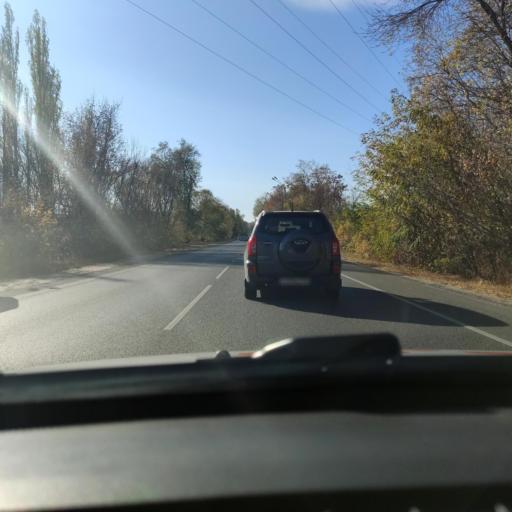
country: RU
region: Voronezj
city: Maslovka
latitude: 51.5936
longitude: 39.1760
